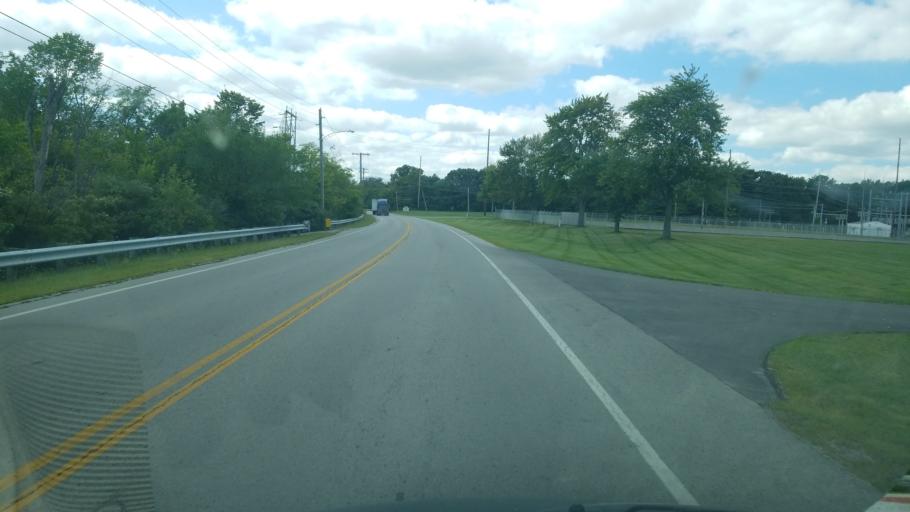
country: US
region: Ohio
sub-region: Henry County
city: Napoleon
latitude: 41.4104
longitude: -84.0928
